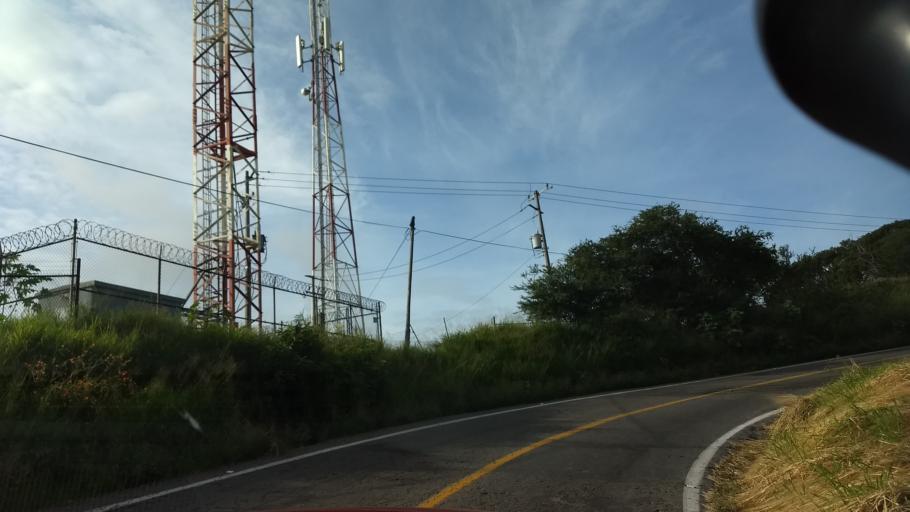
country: MX
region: Jalisco
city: Tuxpan
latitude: 19.5226
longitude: -103.4410
